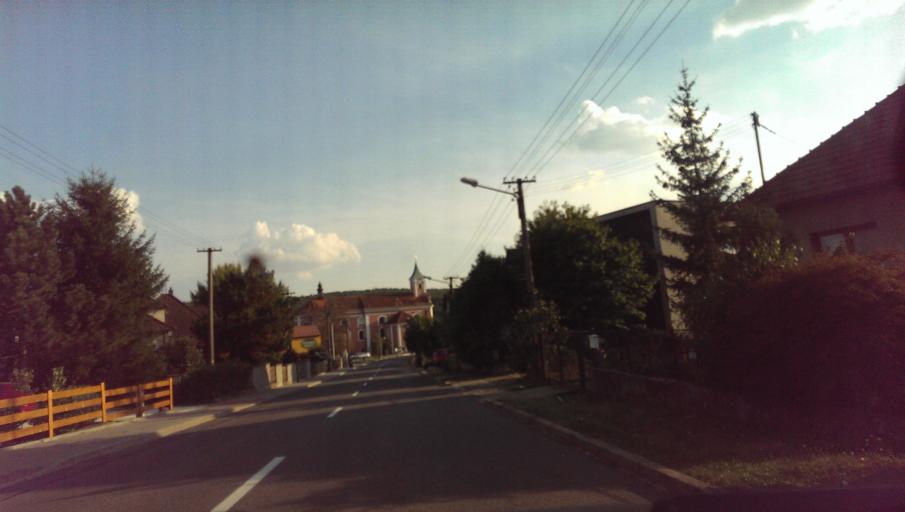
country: CZ
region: Zlin
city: Lukov
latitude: 49.2645
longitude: 17.7158
